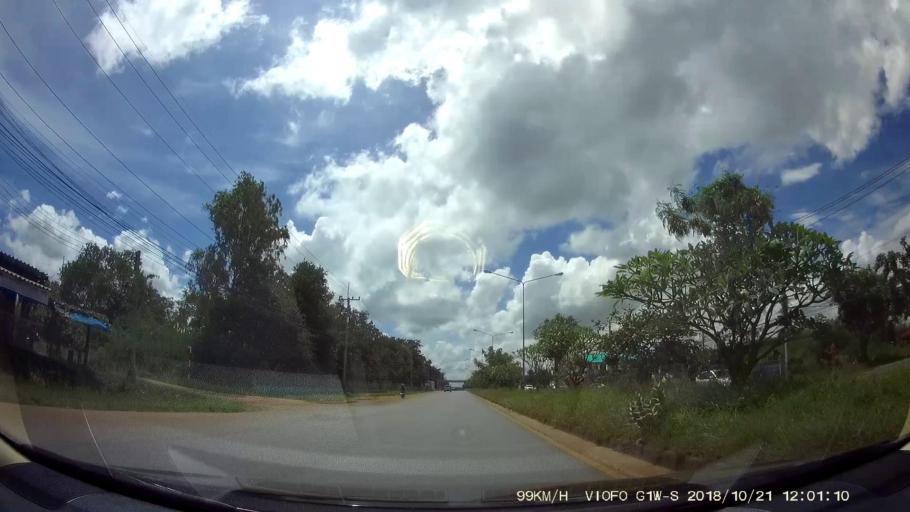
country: TH
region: Chaiyaphum
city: Chatturat
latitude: 15.5418
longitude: 101.8374
